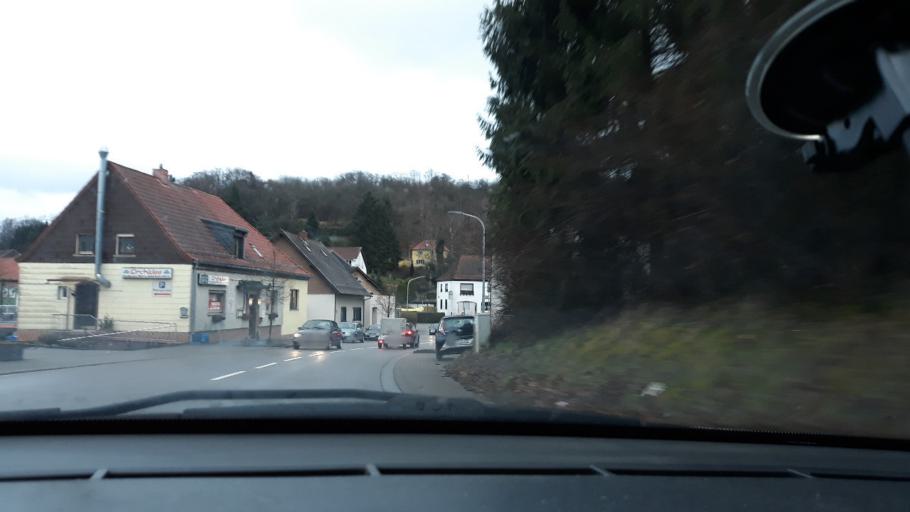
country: DE
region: Saarland
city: Kirkel
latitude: 49.2439
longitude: 7.1924
